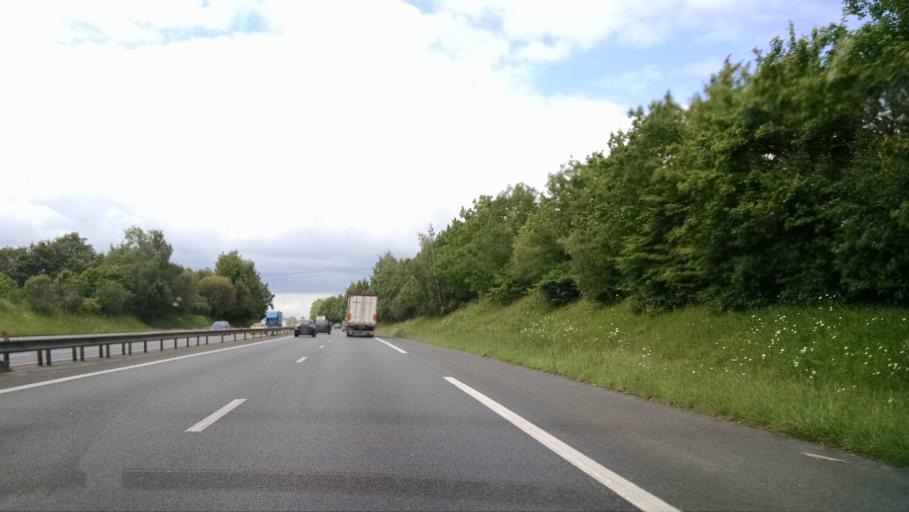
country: FR
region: Pays de la Loire
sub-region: Departement de la Loire-Atlantique
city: Les Sorinieres
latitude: 47.1646
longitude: -1.5126
